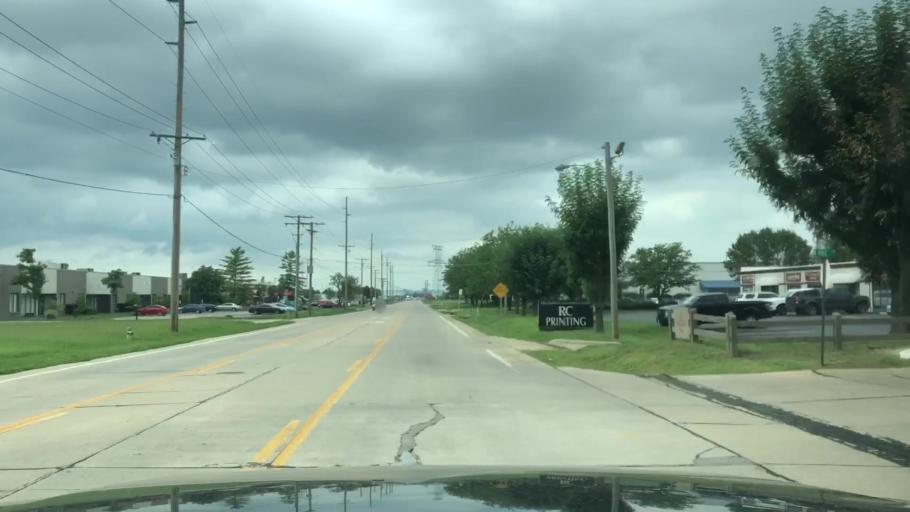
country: US
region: Missouri
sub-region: Saint Charles County
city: Saint Charles
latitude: 38.8215
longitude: -90.5015
